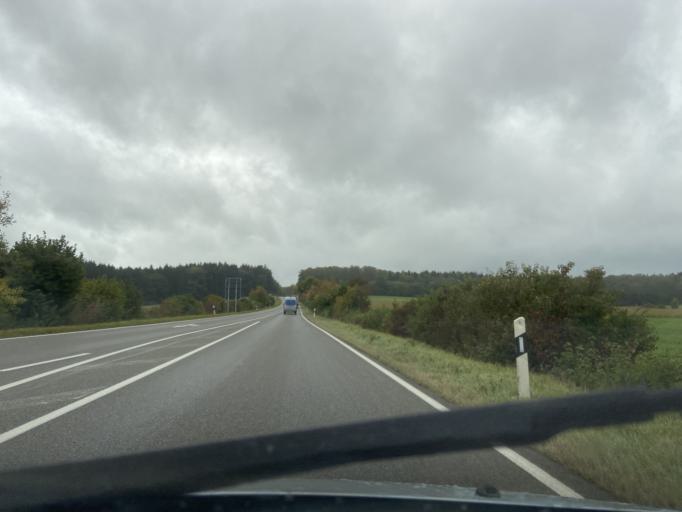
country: DE
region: Baden-Wuerttemberg
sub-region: Tuebingen Region
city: Messkirch
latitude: 47.9863
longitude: 9.0645
